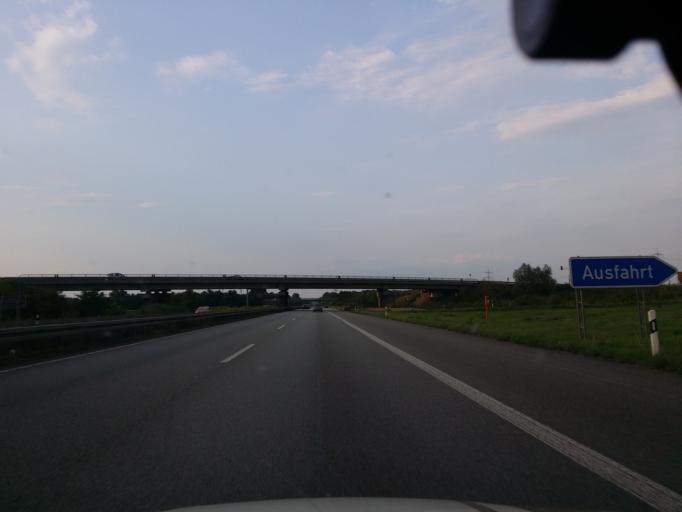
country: DE
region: Hesse
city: Pfungstadt
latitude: 49.8017
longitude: 8.5712
